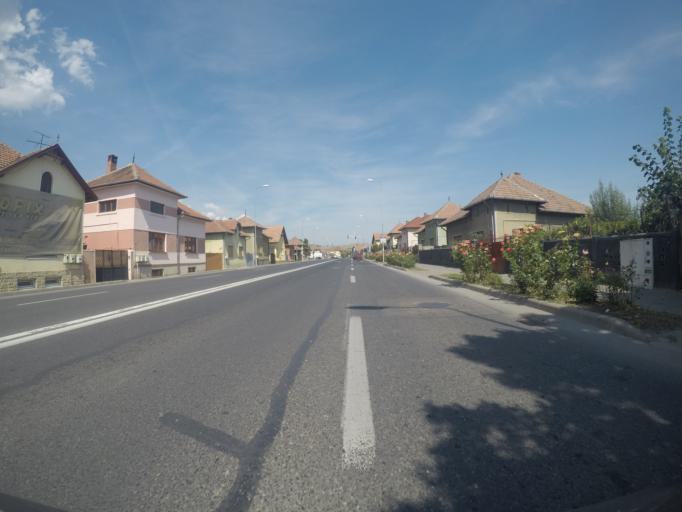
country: RO
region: Alba
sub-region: Municipiul Alba Iulia
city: Alba Iulia
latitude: 46.0817
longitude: 23.5845
